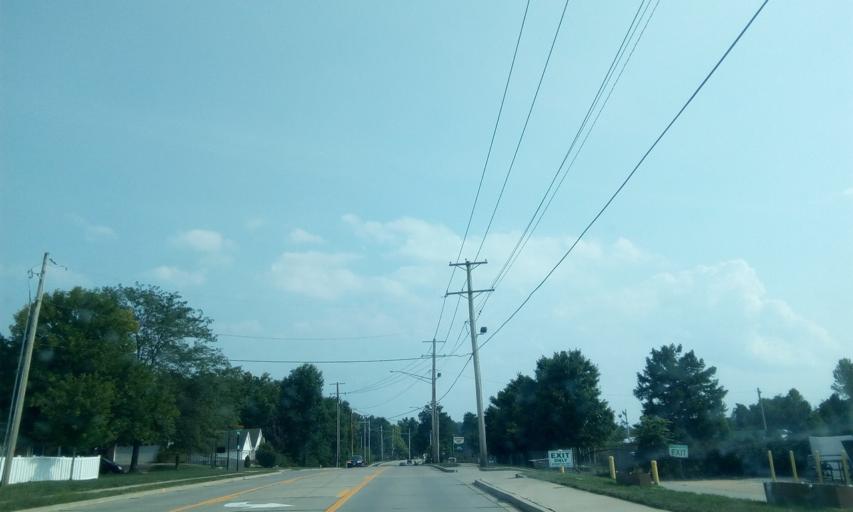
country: US
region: Missouri
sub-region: Saint Louis County
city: Town and Country
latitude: 38.5872
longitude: -90.4685
